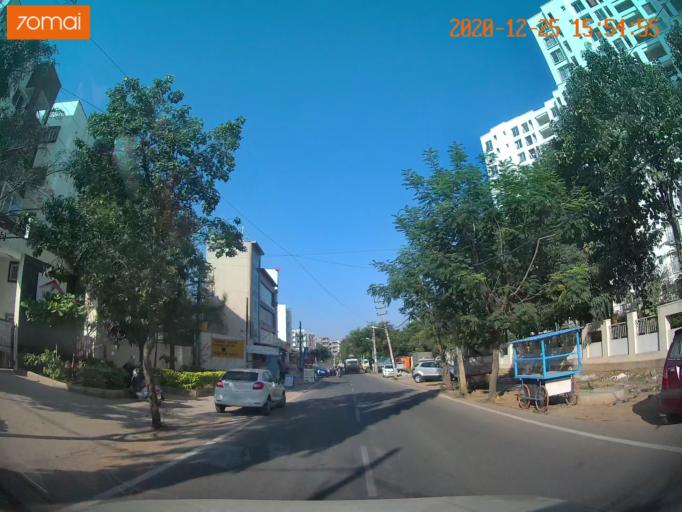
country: IN
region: Karnataka
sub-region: Bangalore Urban
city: Bangalore
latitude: 12.8592
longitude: 77.6121
